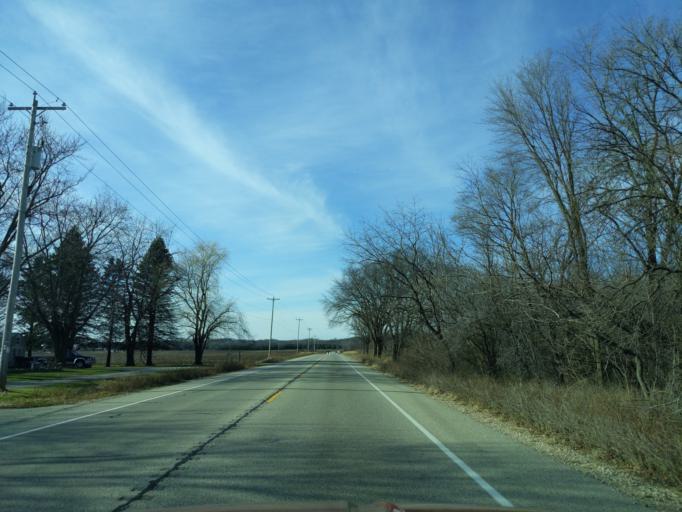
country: US
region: Wisconsin
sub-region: Jefferson County
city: Palmyra
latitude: 42.7967
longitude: -88.6314
